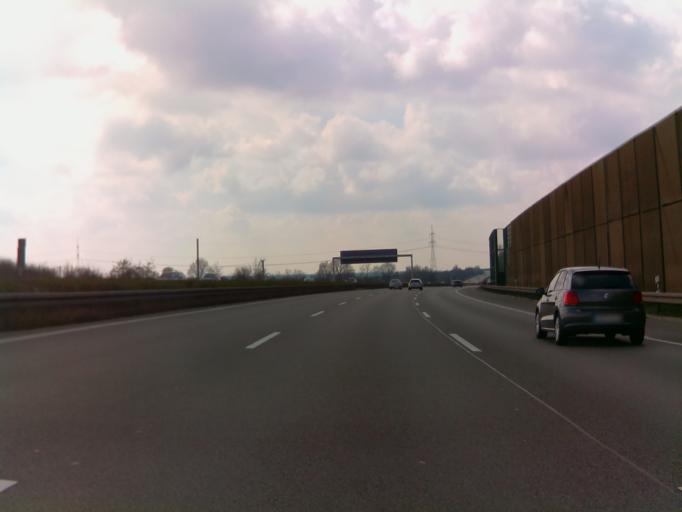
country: DE
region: Thuringia
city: Walpernhain
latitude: 51.0359
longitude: 11.9404
